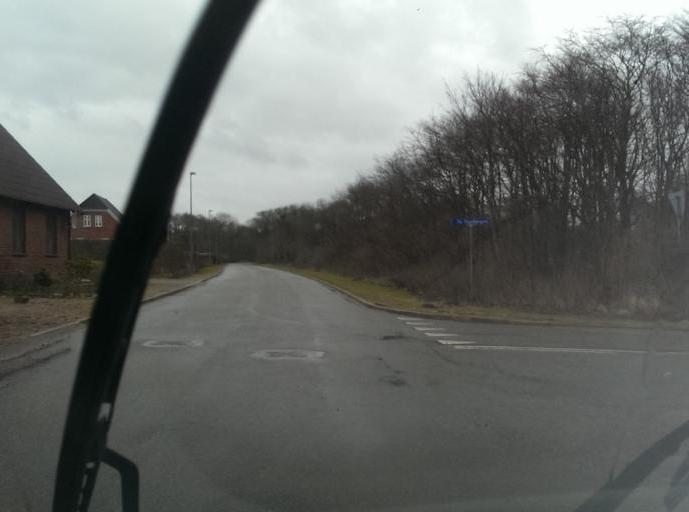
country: DK
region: Central Jutland
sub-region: Ringkobing-Skjern Kommune
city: Skjern
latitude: 56.0001
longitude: 8.4207
